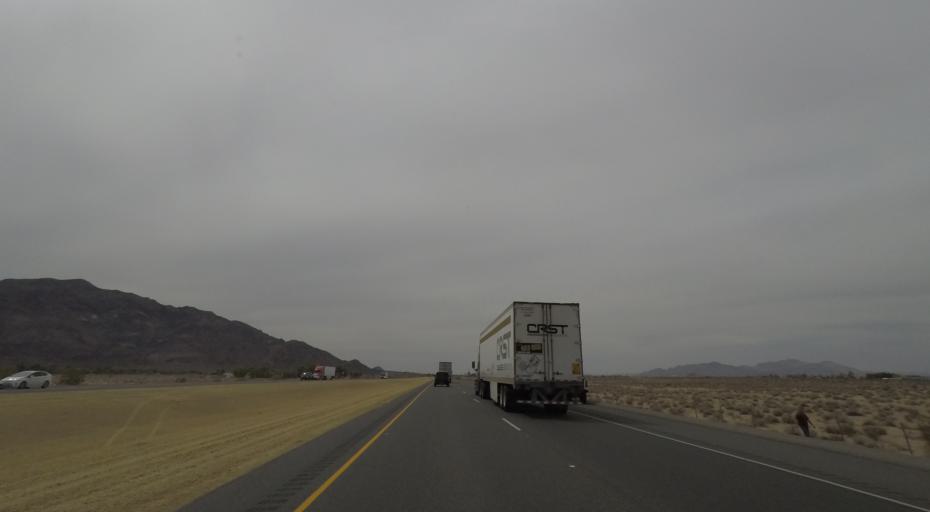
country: US
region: California
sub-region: San Bernardino County
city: Barstow
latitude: 34.8229
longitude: -116.6460
